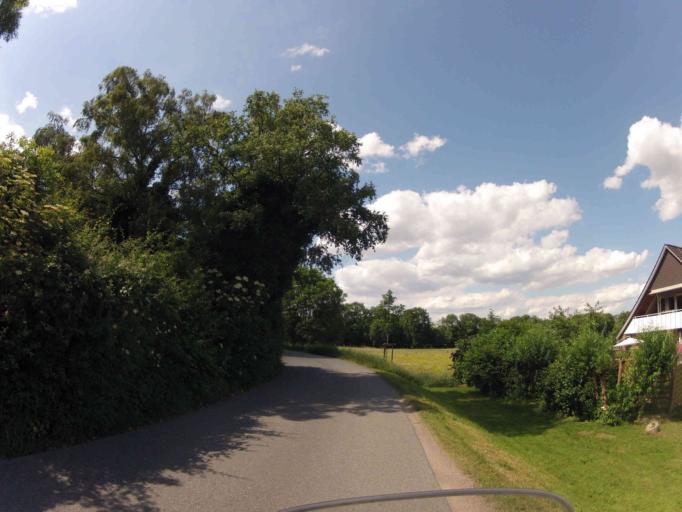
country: DE
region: Hamburg
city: Rothenburgsort
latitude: 53.4789
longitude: 10.0987
